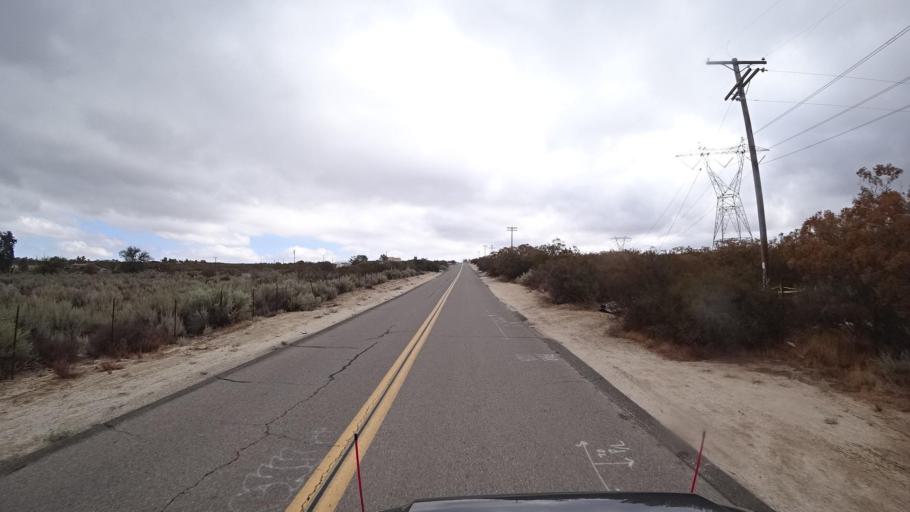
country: US
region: California
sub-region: San Diego County
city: Campo
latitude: 32.6047
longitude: -116.3461
